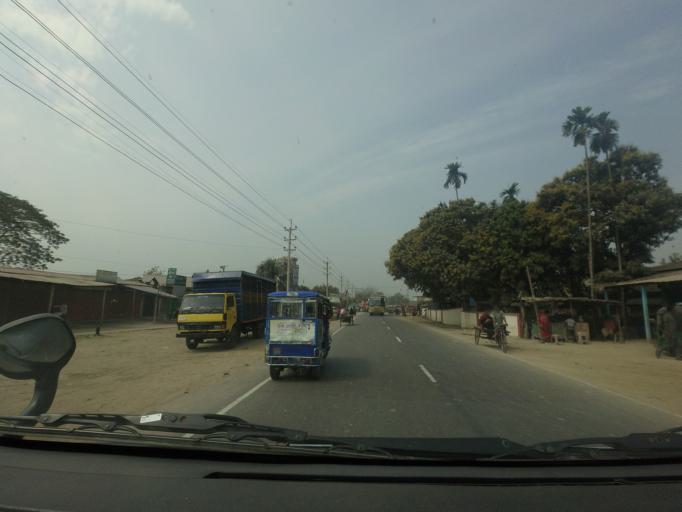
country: BD
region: Dhaka
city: Bajitpur
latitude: 24.2086
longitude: 90.8565
